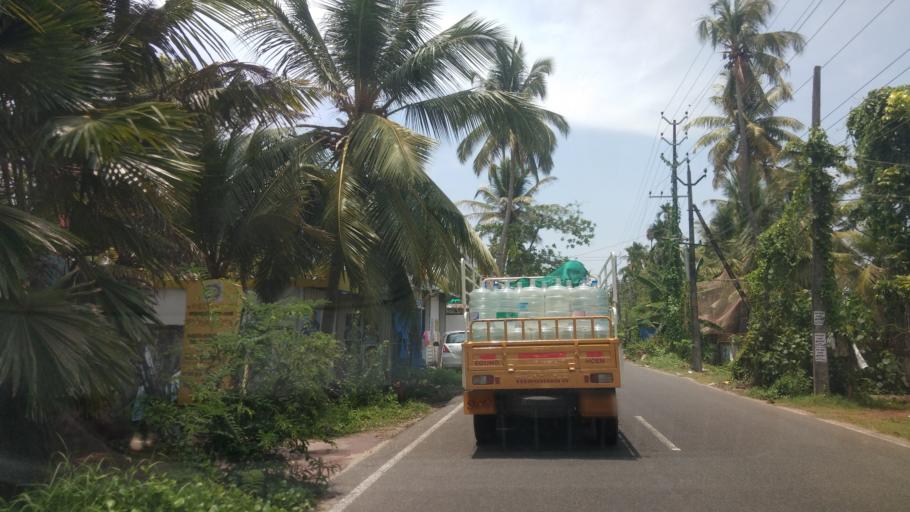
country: IN
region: Kerala
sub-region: Alappuzha
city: Kutiatodu
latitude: 9.8498
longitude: 76.2668
